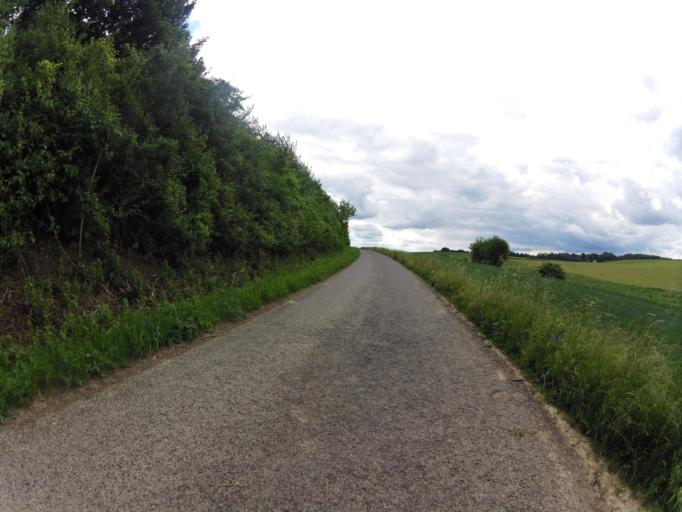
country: DE
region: Bavaria
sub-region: Regierungsbezirk Unterfranken
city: Gaukonigshofen
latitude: 49.6584
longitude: 9.9976
